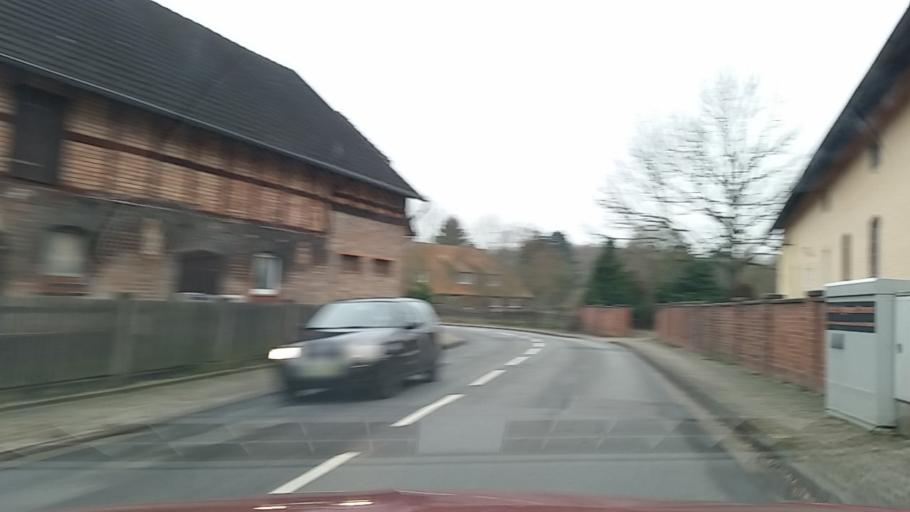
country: DE
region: Lower Saxony
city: Wasbuttel
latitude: 52.3828
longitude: 10.5901
